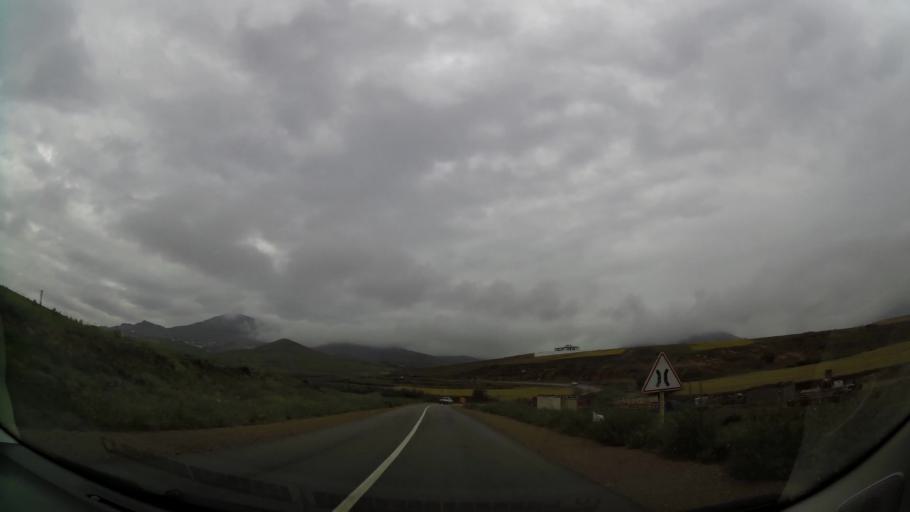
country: MA
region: Oriental
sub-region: Nador
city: Nador
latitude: 35.1519
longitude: -3.0395
